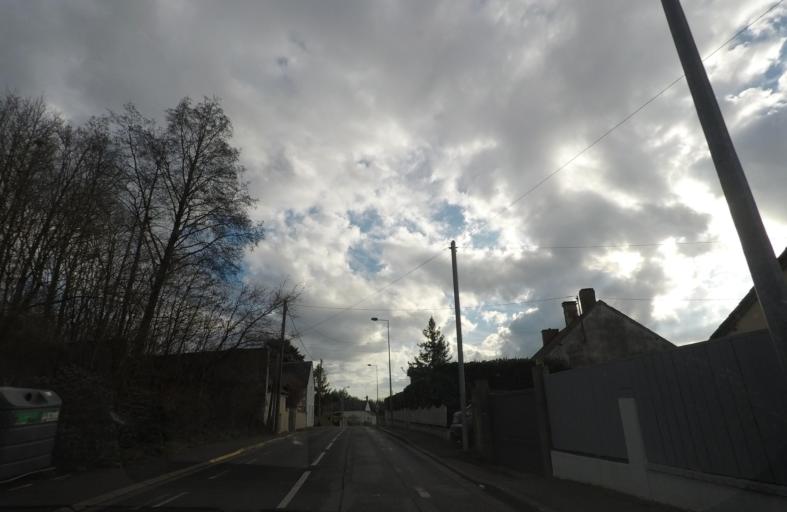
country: FR
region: Centre
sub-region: Departement du Cher
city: Bourges
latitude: 47.0596
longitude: 2.4020
